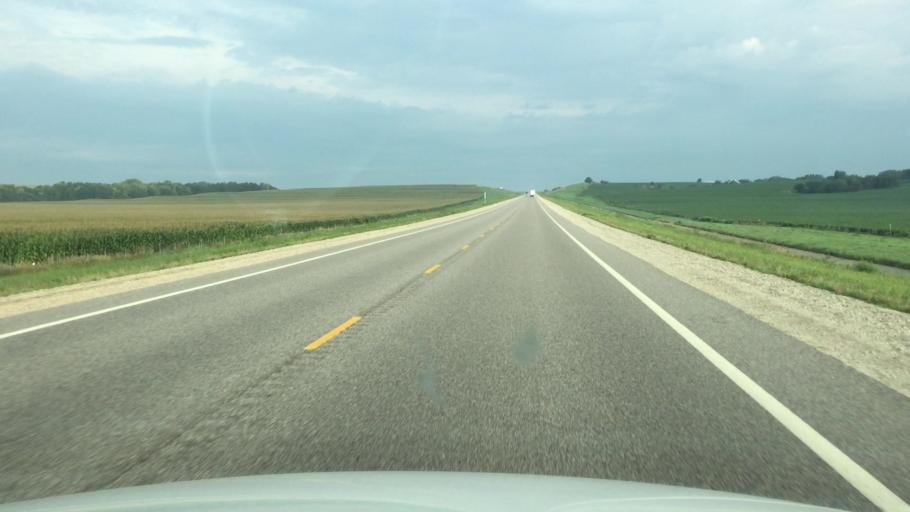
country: US
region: Kansas
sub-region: Doniphan County
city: Highland
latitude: 39.8176
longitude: -95.2060
